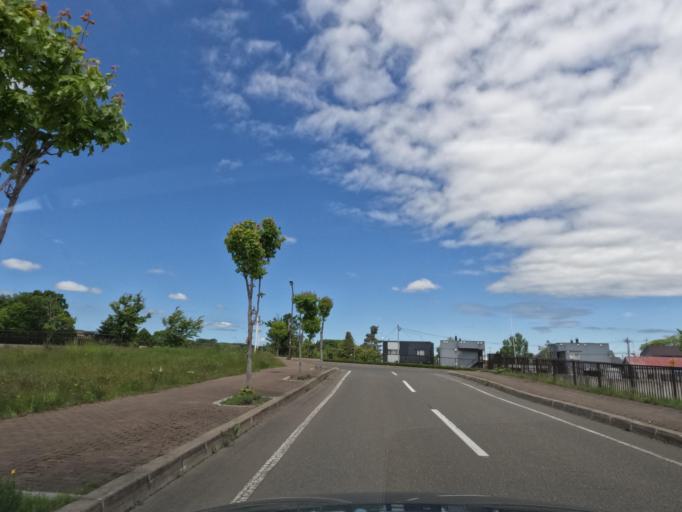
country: JP
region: Hokkaido
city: Shimo-furano
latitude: 43.4605
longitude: 142.4639
